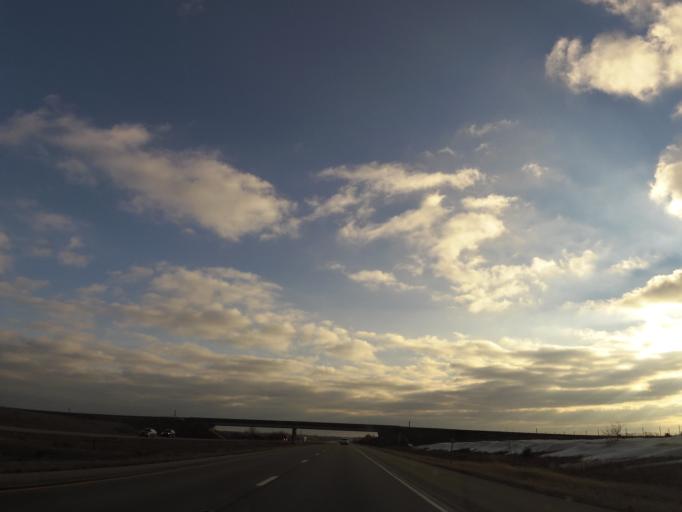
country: US
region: Illinois
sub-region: Ogle County
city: Rochelle
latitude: 41.8203
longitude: -89.0100
